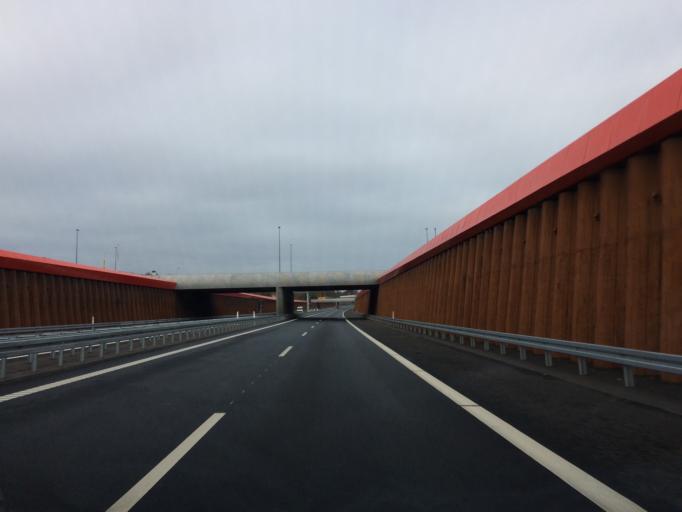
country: DK
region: Central Jutland
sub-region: Silkeborg Kommune
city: Silkeborg
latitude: 56.1863
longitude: 9.5757
